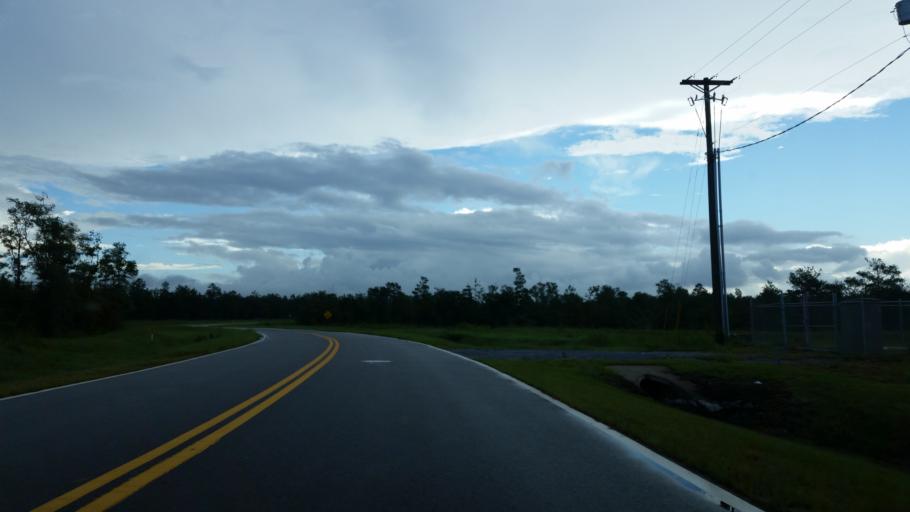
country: US
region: Florida
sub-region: Okaloosa County
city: Crestview
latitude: 30.7350
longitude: -86.3466
